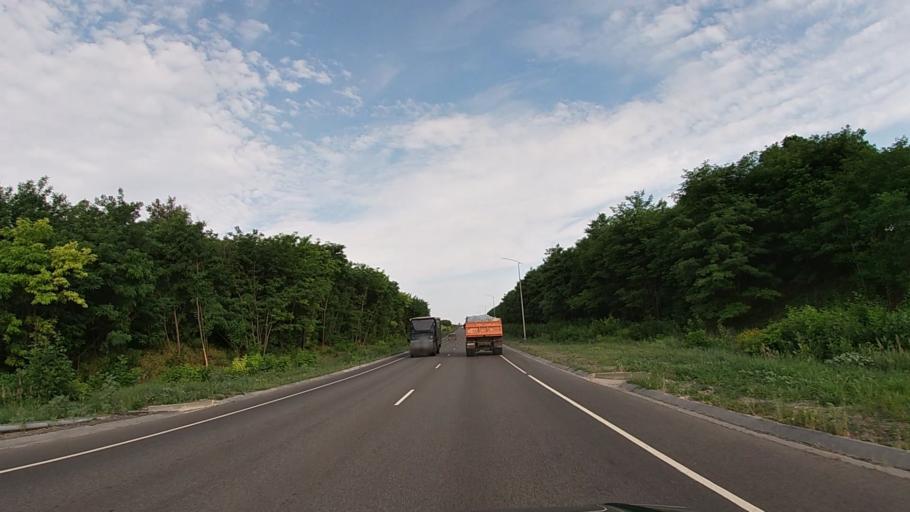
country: RU
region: Belgorod
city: Severnyy
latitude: 50.6685
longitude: 36.4899
